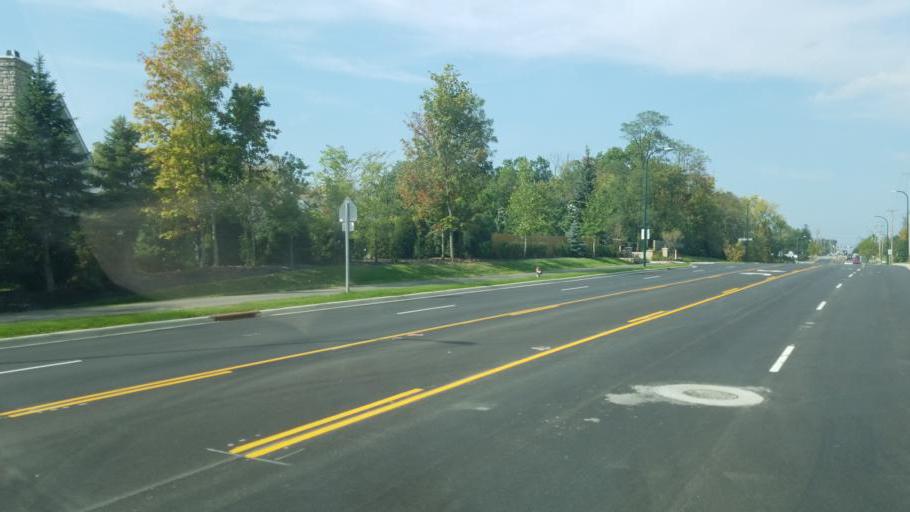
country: US
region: Ohio
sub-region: Franklin County
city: Gahanna
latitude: 40.0333
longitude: -82.8653
